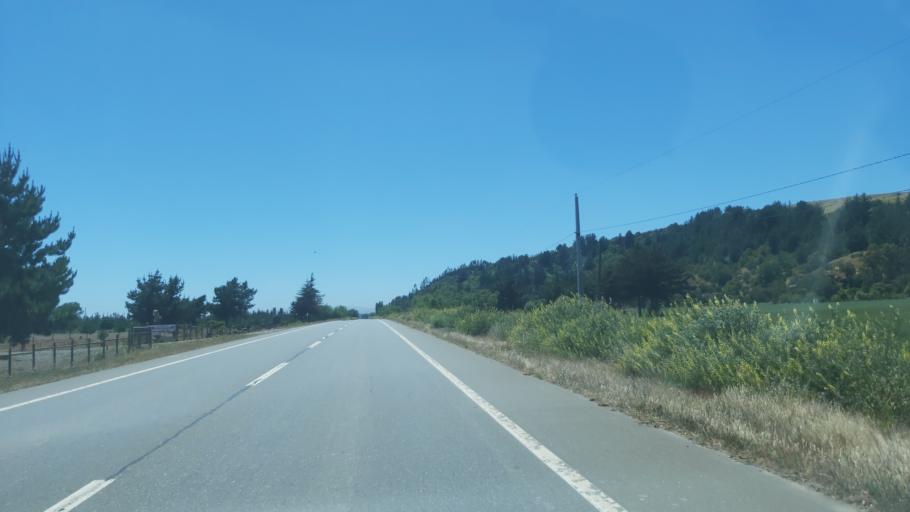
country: CL
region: Maule
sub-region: Provincia de Talca
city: Constitucion
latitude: -35.1683
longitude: -72.2640
